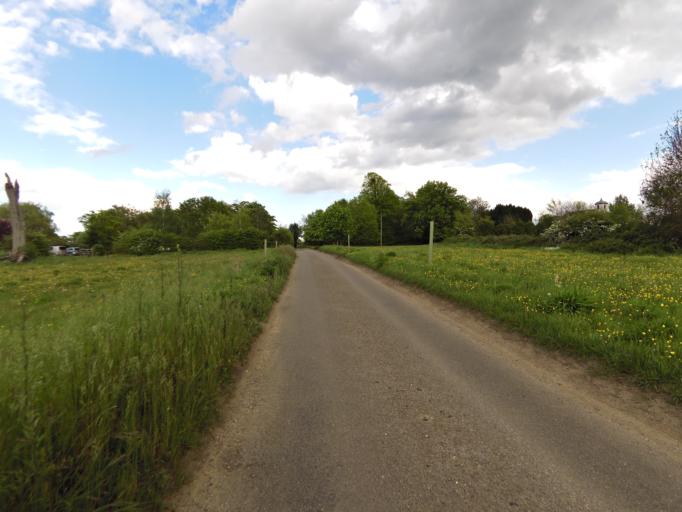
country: GB
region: England
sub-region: Suffolk
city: Elmswell
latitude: 52.2045
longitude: 0.9293
